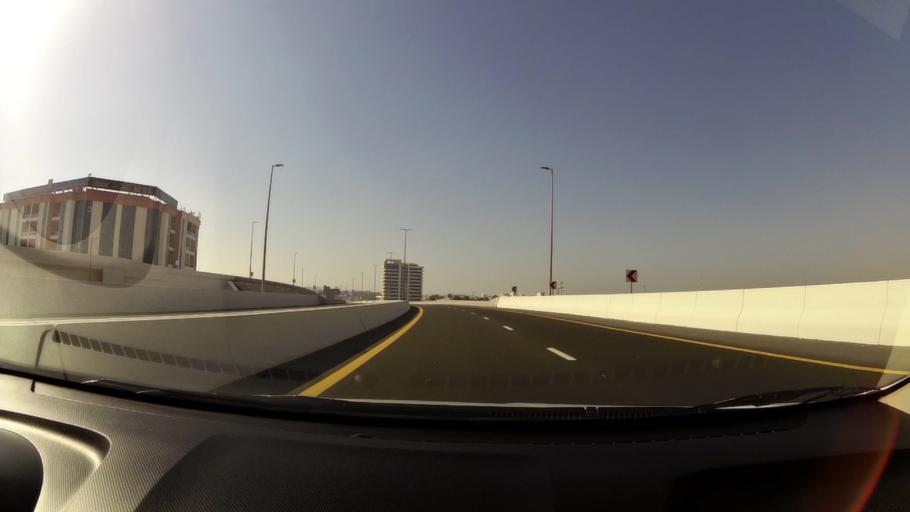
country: AE
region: Umm al Qaywayn
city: Umm al Qaywayn
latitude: 25.4943
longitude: 55.5531
